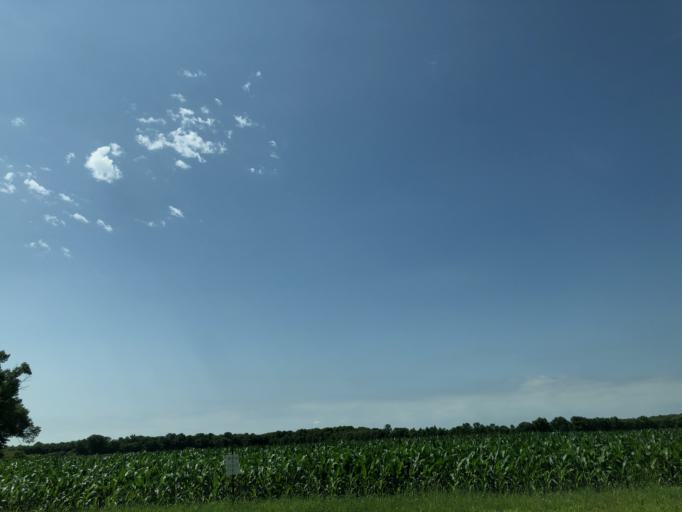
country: US
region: Minnesota
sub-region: Douglas County
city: Alexandria
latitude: 45.9370
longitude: -95.3812
